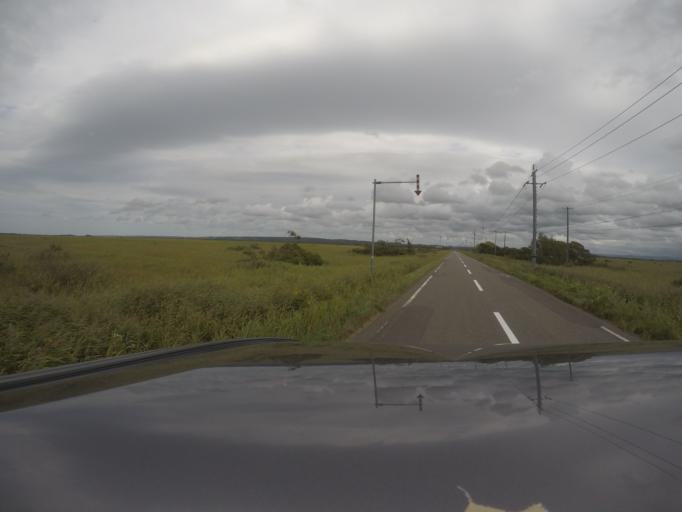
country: JP
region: Hokkaido
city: Makubetsu
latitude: 45.0076
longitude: 141.7221
